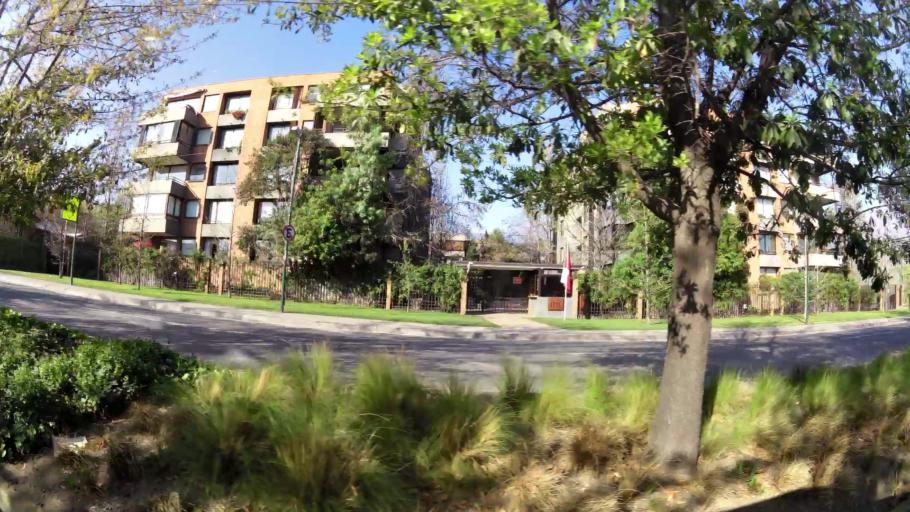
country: CL
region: Santiago Metropolitan
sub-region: Provincia de Santiago
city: Villa Presidente Frei, Nunoa, Santiago, Chile
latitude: -33.3557
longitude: -70.5110
